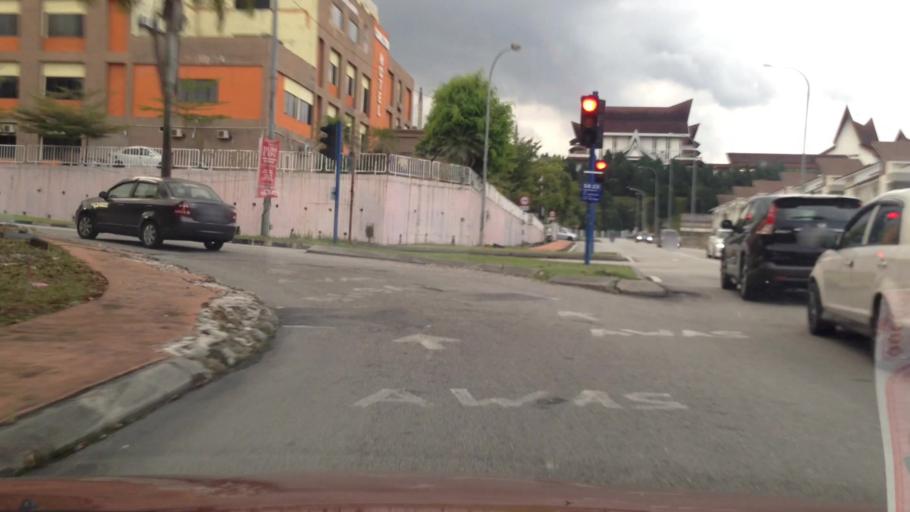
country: MY
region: Selangor
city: Shah Alam
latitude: 3.0729
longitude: 101.5386
